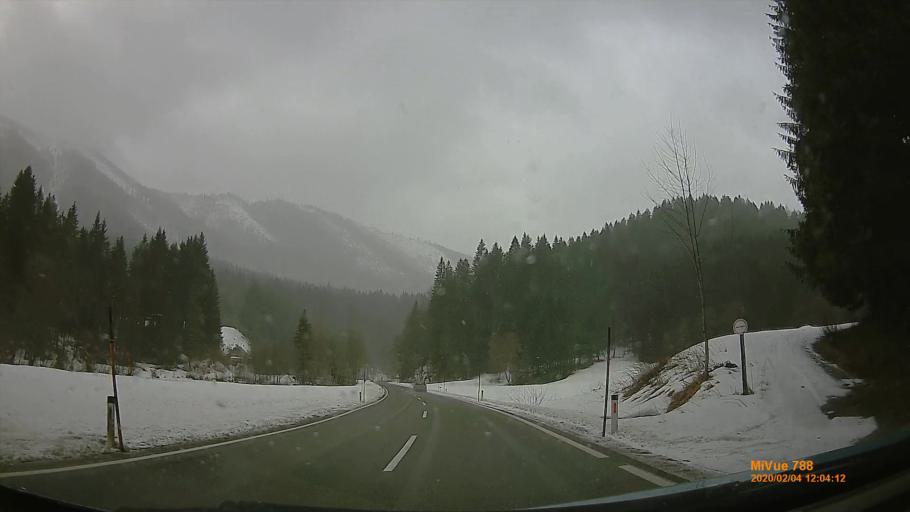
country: AT
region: Styria
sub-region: Politischer Bezirk Bruck-Muerzzuschlag
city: Muerzsteg
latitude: 47.7711
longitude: 15.4480
